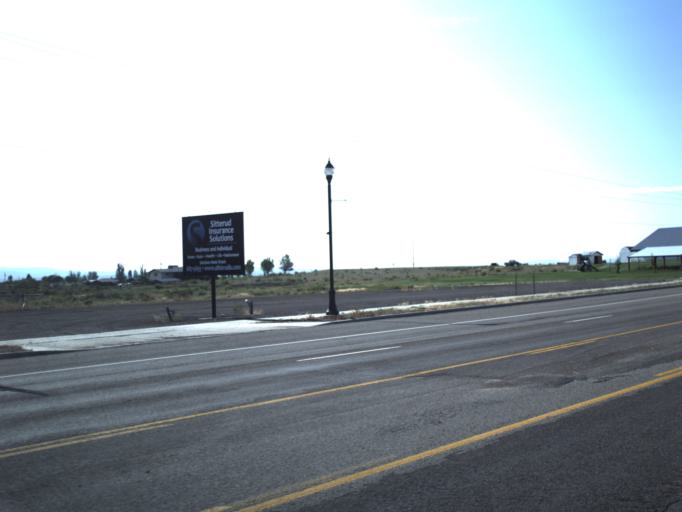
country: US
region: Utah
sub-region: Emery County
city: Huntington
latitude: 39.3203
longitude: -110.9646
